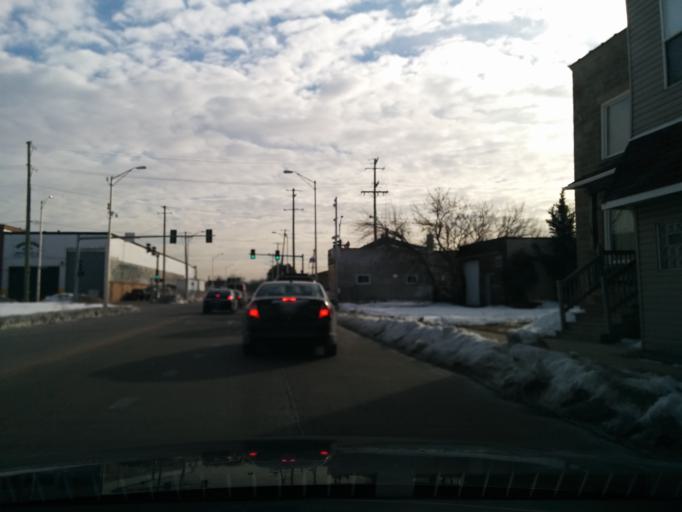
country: US
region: Illinois
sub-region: Cook County
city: Maywood
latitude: 41.8880
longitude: -87.8451
